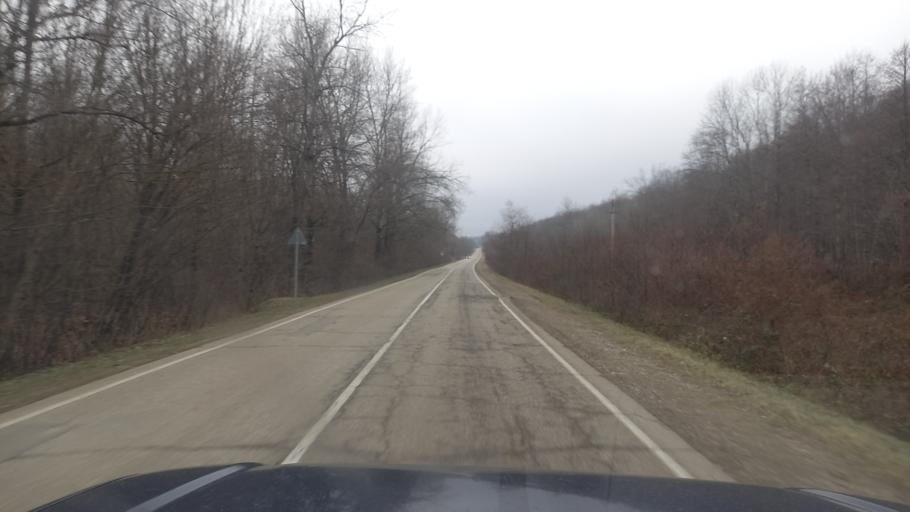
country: RU
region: Krasnodarskiy
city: Neftegorsk
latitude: 44.2822
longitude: 39.7991
